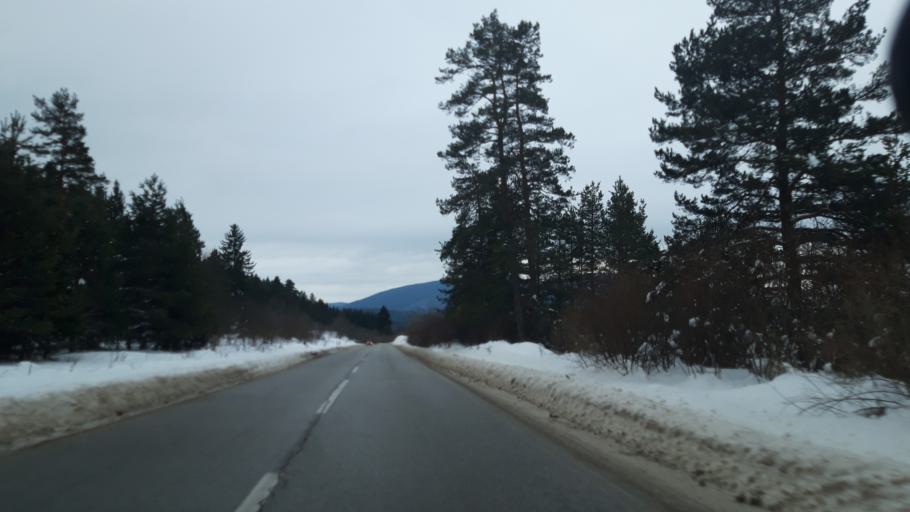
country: BA
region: Republika Srpska
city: Han Pijesak
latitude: 44.0228
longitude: 18.8821
